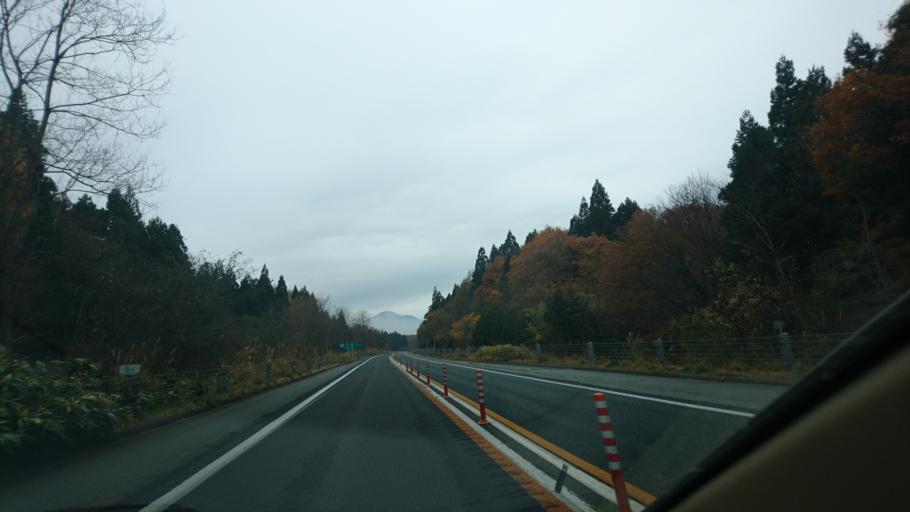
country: JP
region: Iwate
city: Kitakami
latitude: 39.2817
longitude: 141.0070
